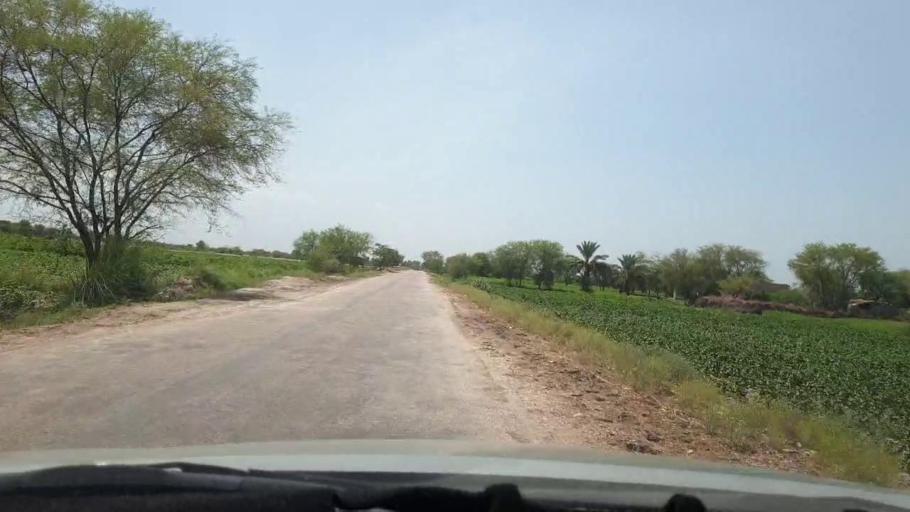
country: PK
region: Sindh
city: Pano Aqil
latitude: 27.6635
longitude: 69.1473
